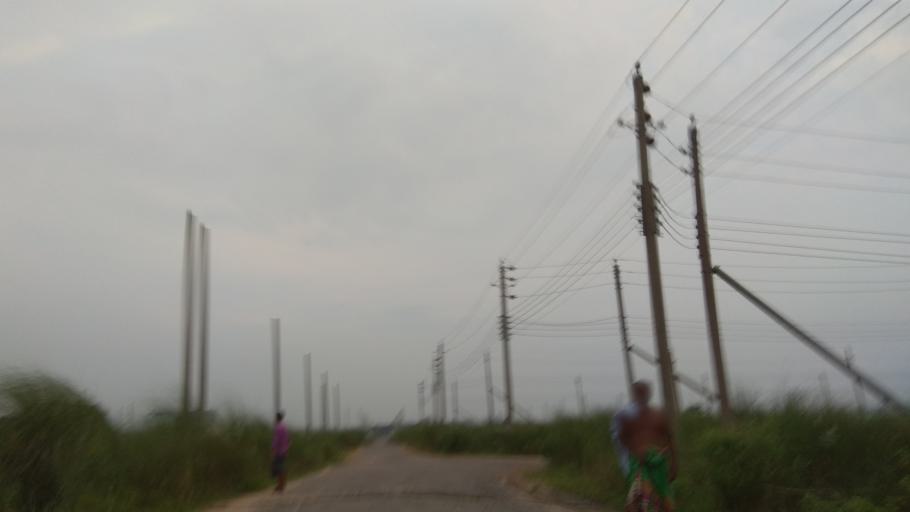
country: BD
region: Dhaka
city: Tungi
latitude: 23.8575
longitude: 90.3692
